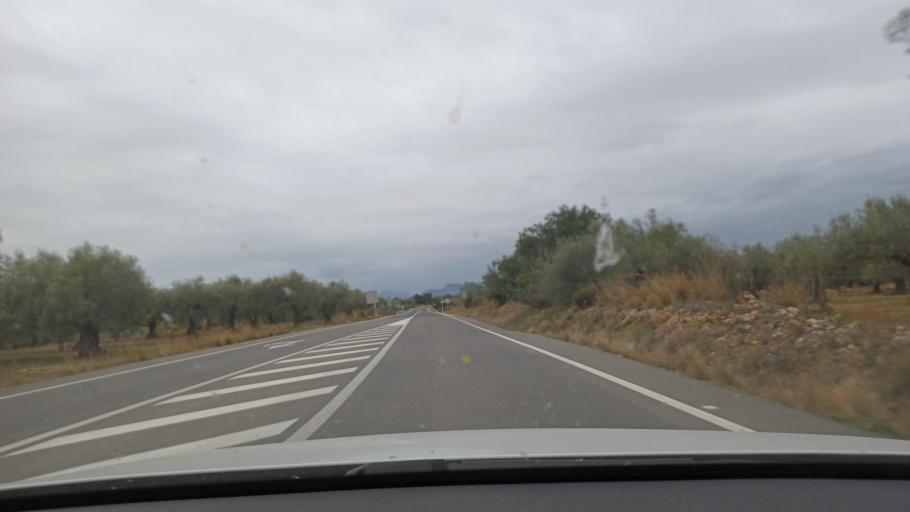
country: ES
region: Catalonia
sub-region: Provincia de Tarragona
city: Mas de Barberans
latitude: 40.6409
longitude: 0.3529
